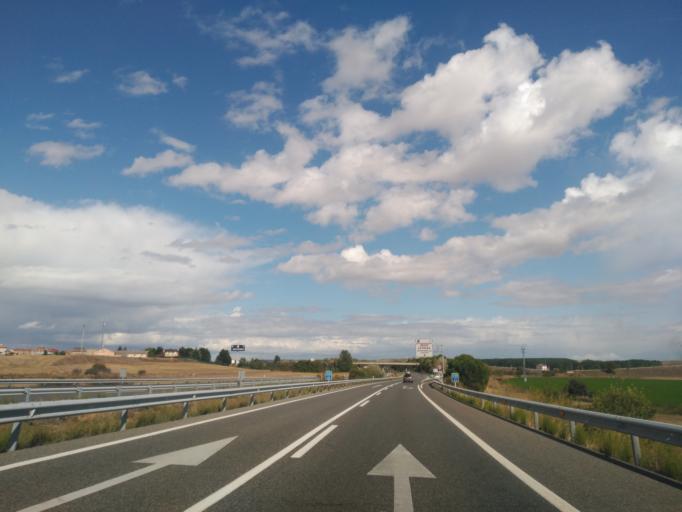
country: ES
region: Castille and Leon
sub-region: Provincia de Burgos
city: Estepar
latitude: 42.2730
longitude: -3.9026
